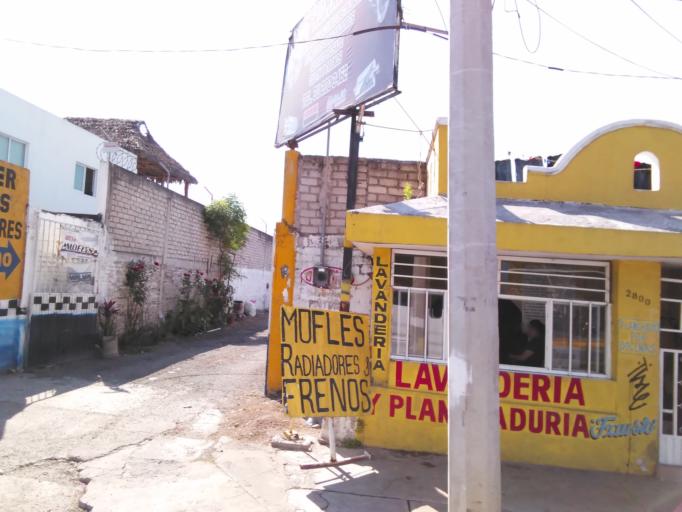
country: MX
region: Nayarit
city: Xalisco
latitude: 21.4740
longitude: -104.8593
